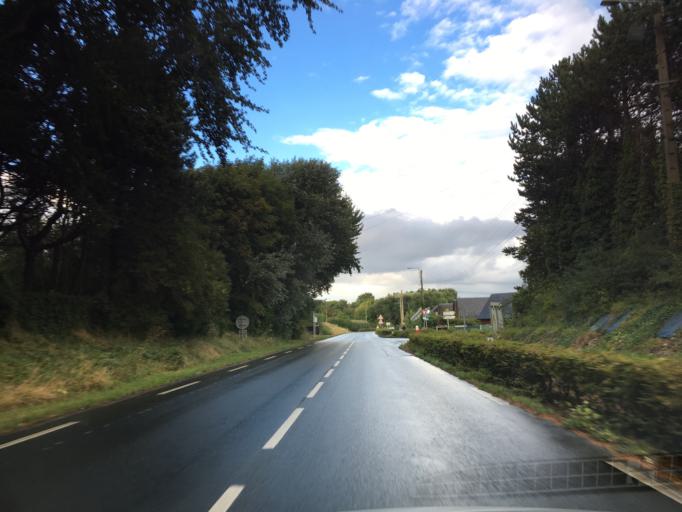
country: FR
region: Lower Normandy
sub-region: Departement du Calvados
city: Merville-Franceville-Plage
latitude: 49.2846
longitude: -0.1790
